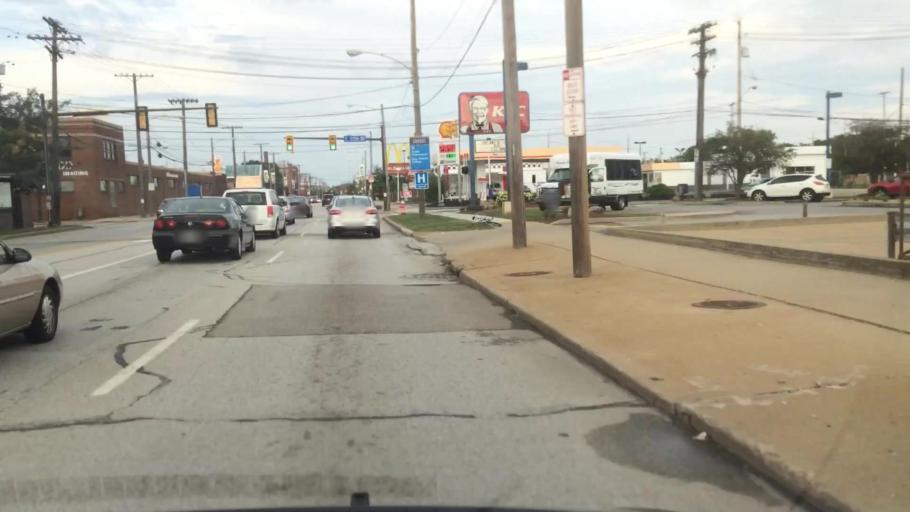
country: US
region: Ohio
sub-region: Cuyahoga County
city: Cleveland
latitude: 41.4998
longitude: -81.6676
